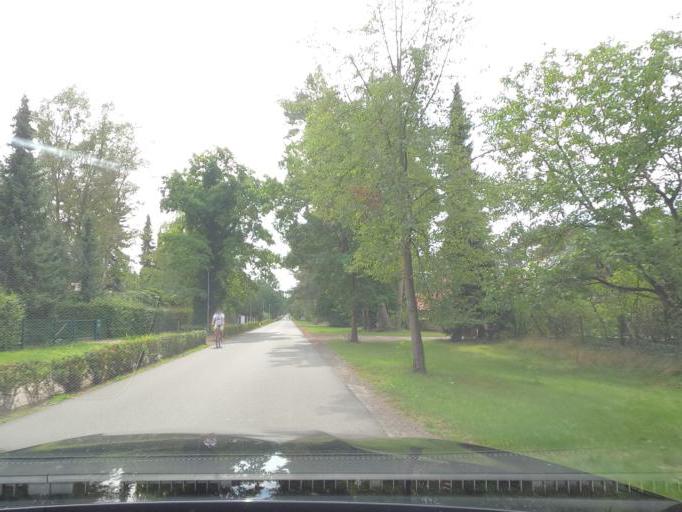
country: DE
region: Lower Saxony
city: Burgdorf
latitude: 52.5122
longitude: 9.9501
